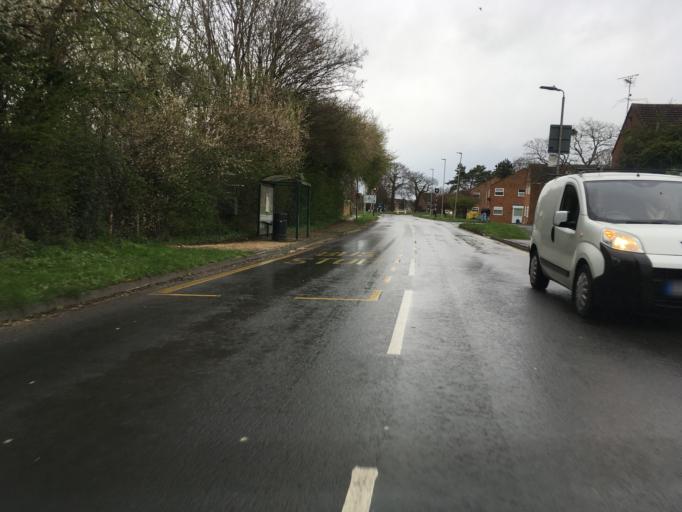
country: GB
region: England
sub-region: Gloucestershire
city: Gloucester
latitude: 51.8218
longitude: -2.2890
